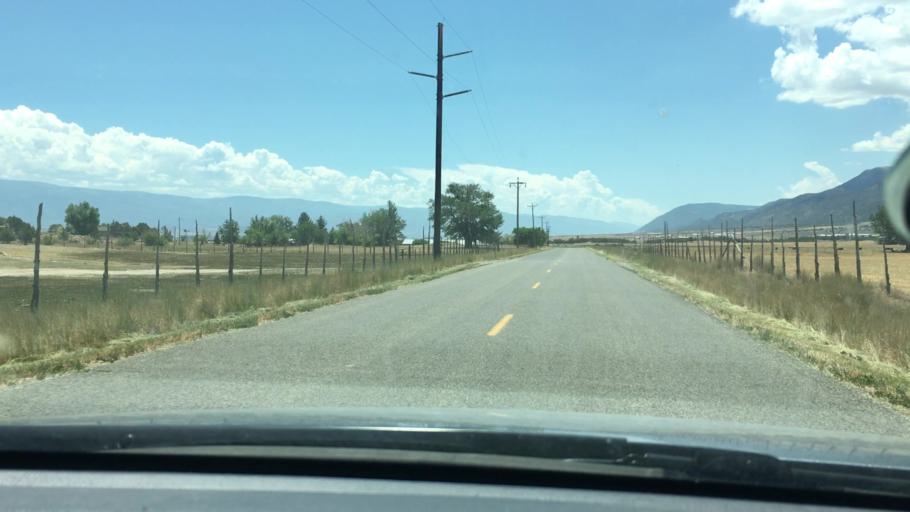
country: US
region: Utah
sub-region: Sanpete County
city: Fountain Green
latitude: 39.6028
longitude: -111.6437
